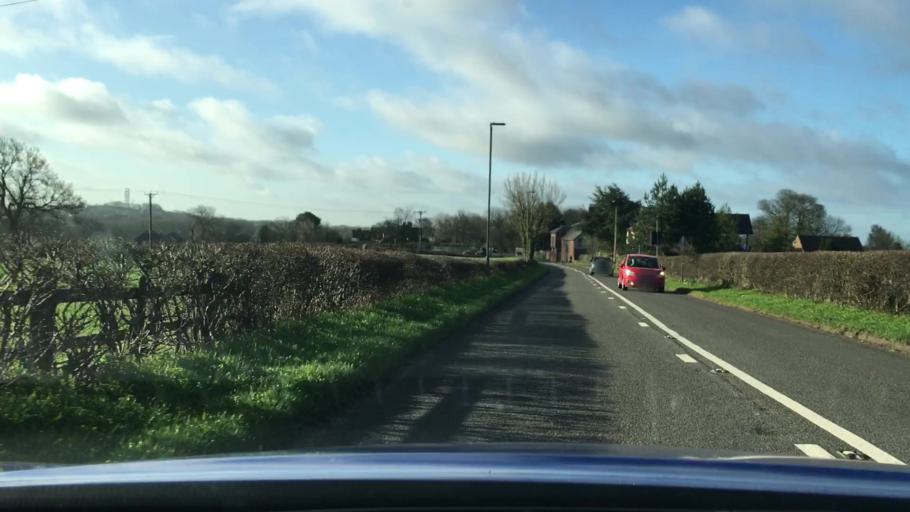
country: GB
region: England
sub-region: Derbyshire
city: Tibshelf
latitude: 53.1555
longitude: -1.3384
